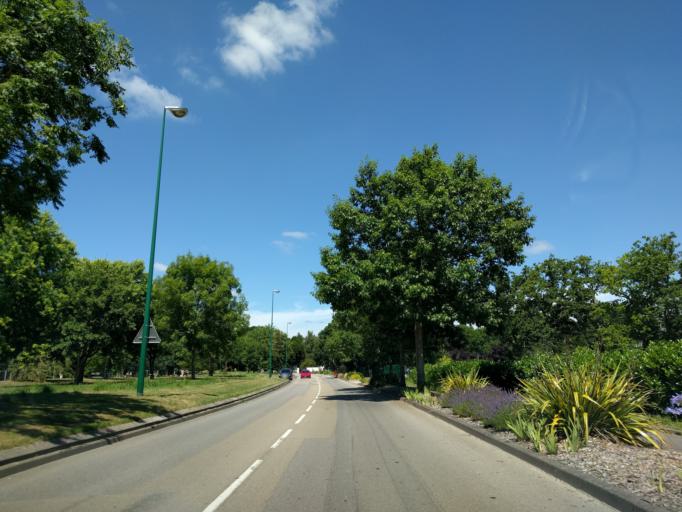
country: FR
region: Brittany
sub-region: Departement du Finistere
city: Quimper
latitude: 47.9759
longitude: -4.0985
